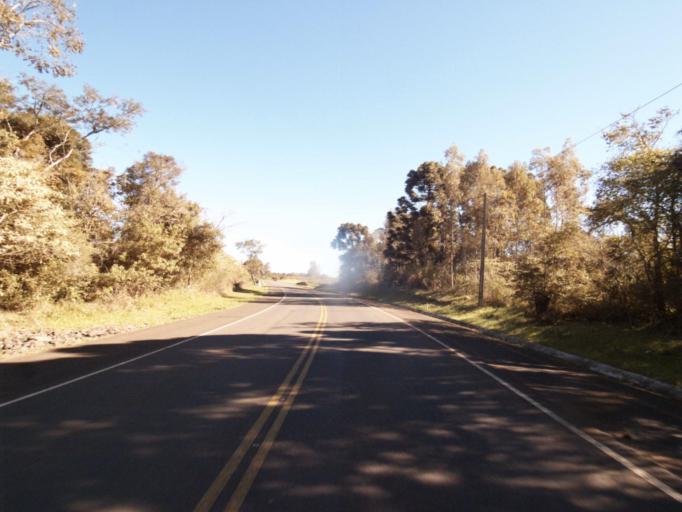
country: AR
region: Misiones
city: Bernardo de Irigoyen
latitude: -26.6698
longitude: -53.5773
